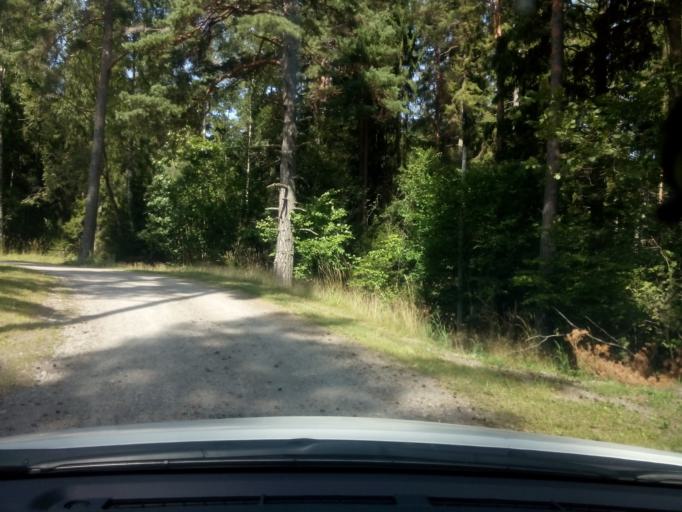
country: SE
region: Soedermanland
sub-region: Trosa Kommun
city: Trosa
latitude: 58.7960
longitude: 17.3836
